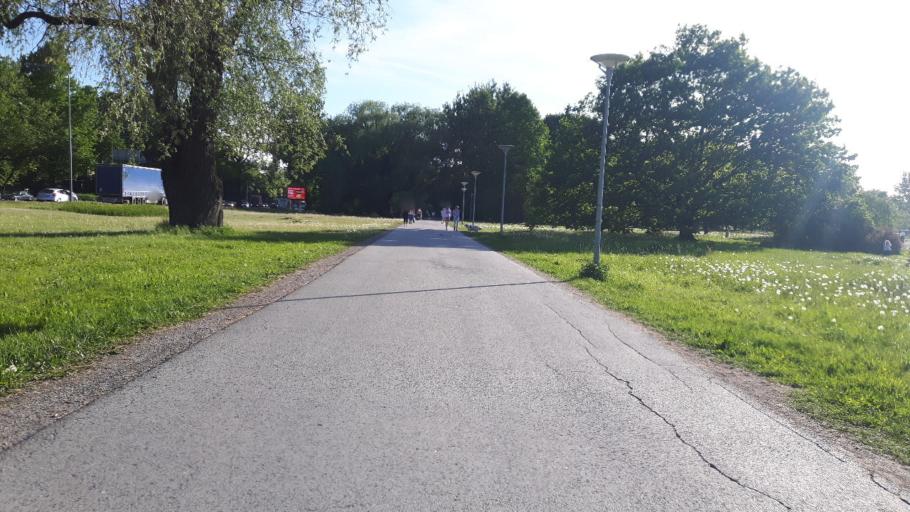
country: EE
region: Harju
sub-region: Tallinna linn
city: Tallinn
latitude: 59.4429
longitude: 24.7911
